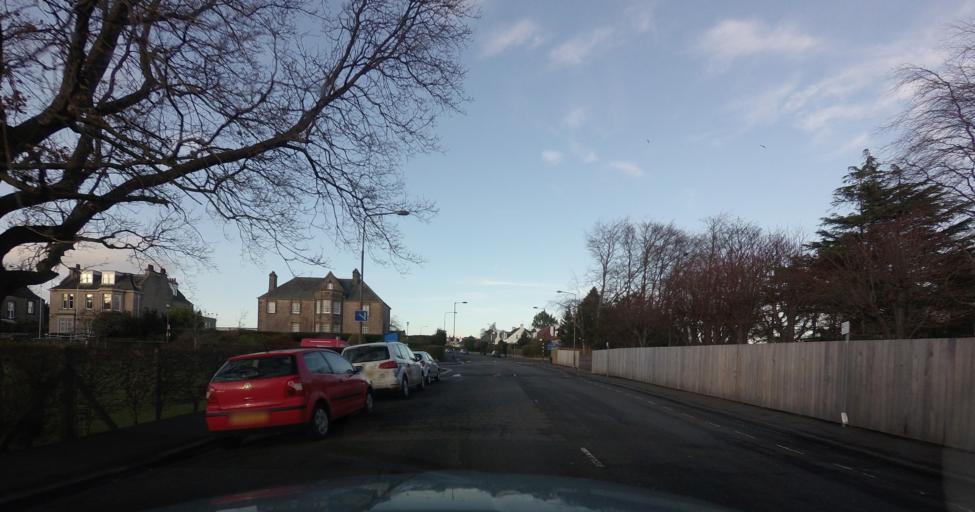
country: GB
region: Scotland
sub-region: Edinburgh
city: Edinburgh
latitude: 55.9680
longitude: -3.2150
